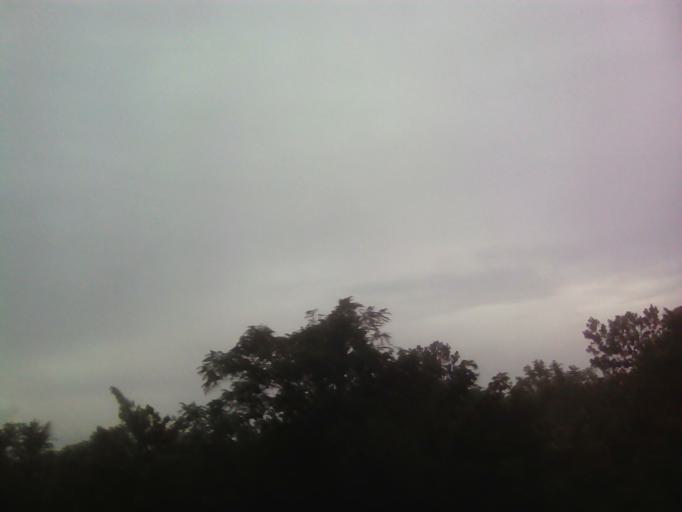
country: MY
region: Kedah
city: Kulim
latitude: 5.4189
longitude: 100.5346
